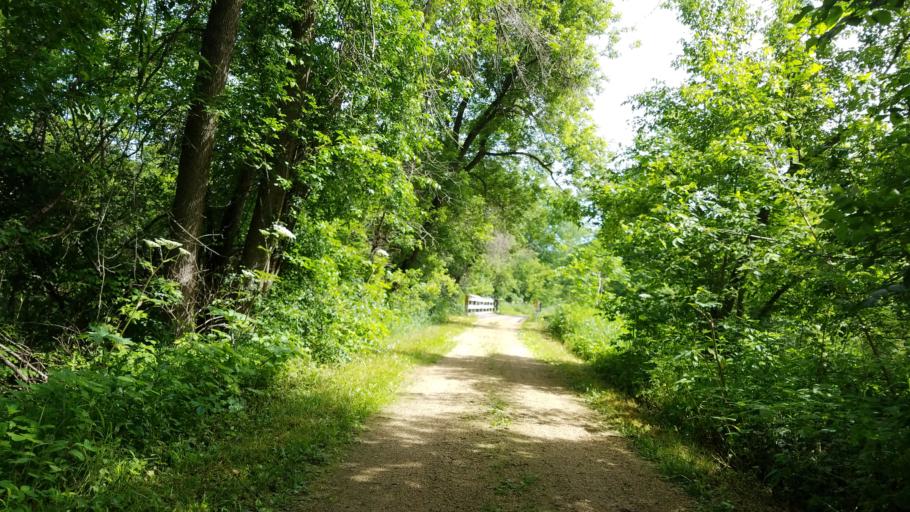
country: US
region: Wisconsin
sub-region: Dunn County
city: Menomonie
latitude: 44.8125
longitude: -91.9505
